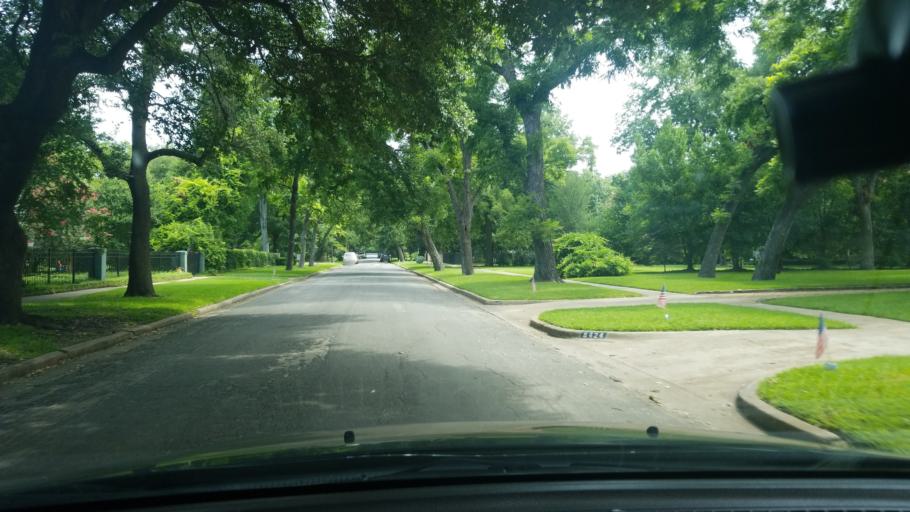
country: US
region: Texas
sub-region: Dallas County
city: Highland Park
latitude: 32.8184
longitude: -96.7161
